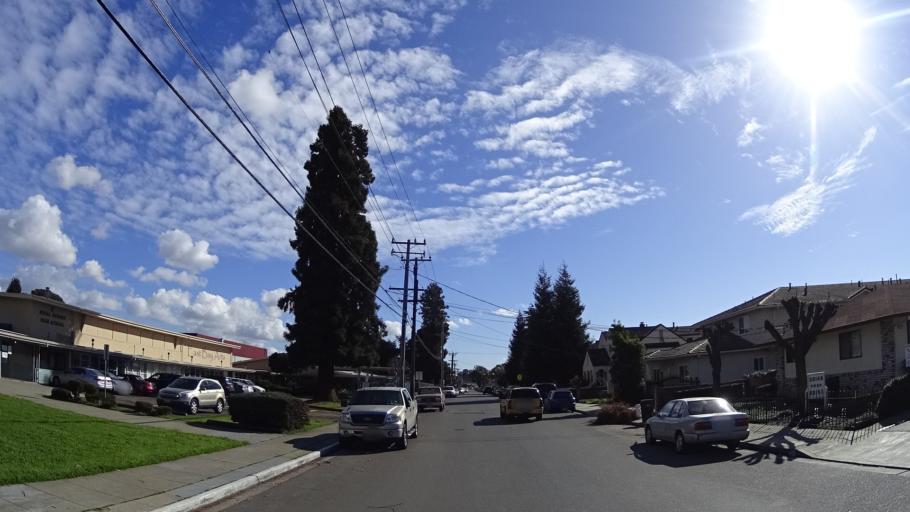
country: US
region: California
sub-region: Alameda County
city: San Lorenzo
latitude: 37.6697
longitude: -122.1155
